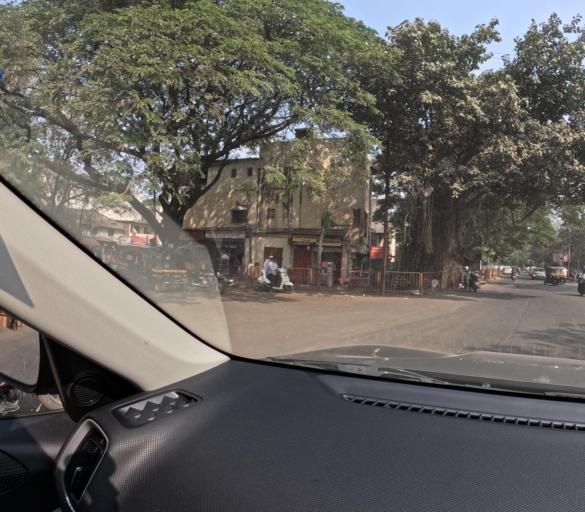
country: IN
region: Maharashtra
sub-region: Pune Division
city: Pune
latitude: 18.5251
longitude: 73.8938
